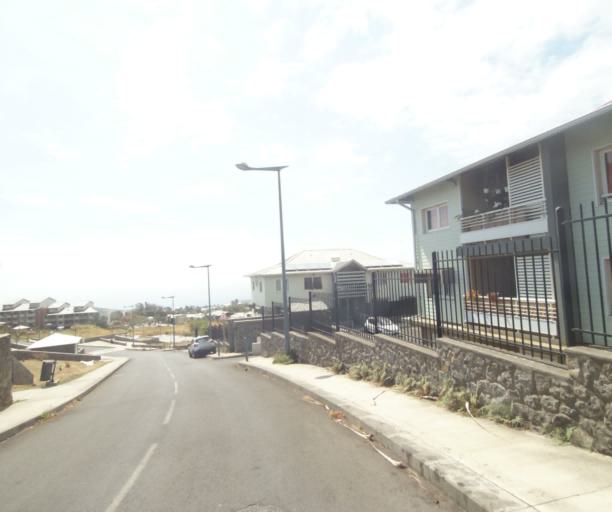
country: RE
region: Reunion
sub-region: Reunion
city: Saint-Paul
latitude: -21.0464
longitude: 55.2617
